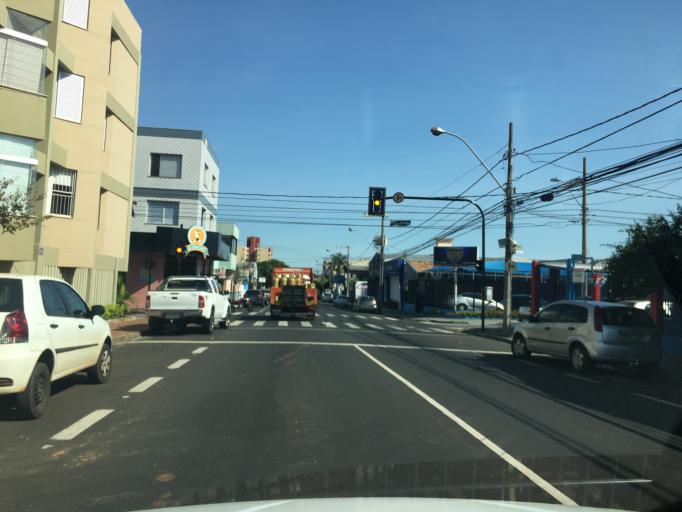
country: BR
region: Minas Gerais
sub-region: Uberlandia
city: Uberlandia
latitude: -18.8970
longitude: -48.2638
